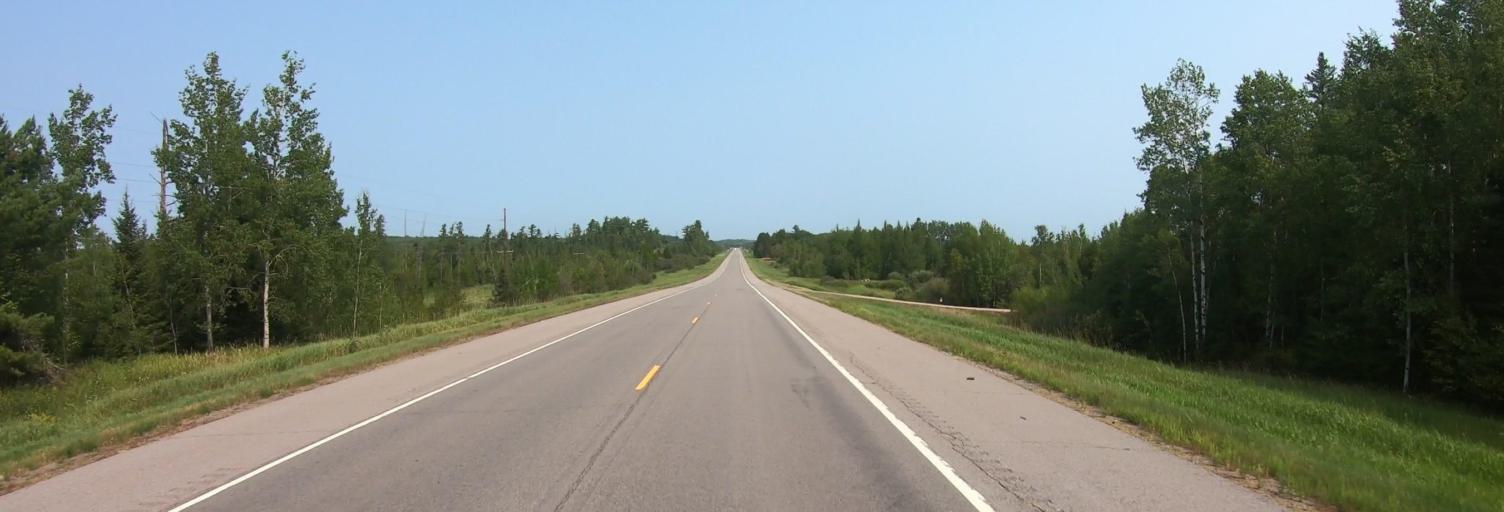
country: US
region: Minnesota
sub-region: Saint Louis County
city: Mountain Iron
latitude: 48.0064
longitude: -92.8308
